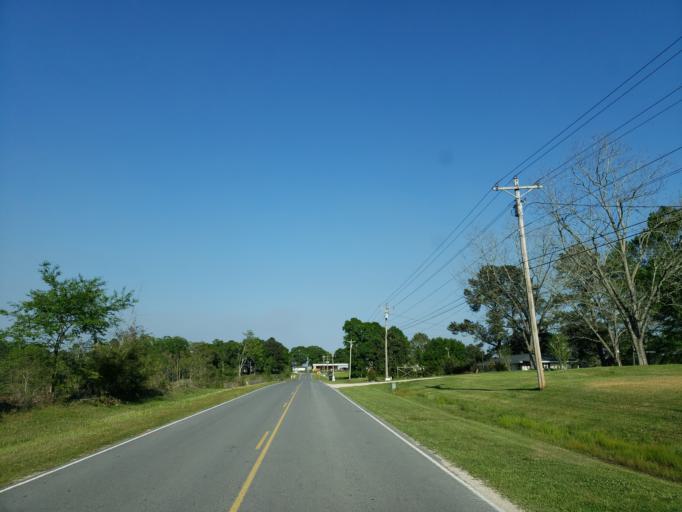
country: US
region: Mississippi
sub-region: Perry County
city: Richton
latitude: 31.4821
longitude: -89.0205
